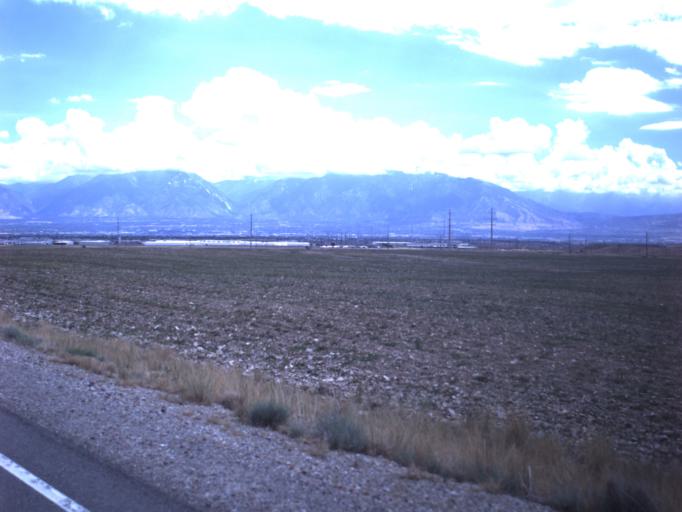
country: US
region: Utah
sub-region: Salt Lake County
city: Herriman
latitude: 40.5684
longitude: -112.0775
